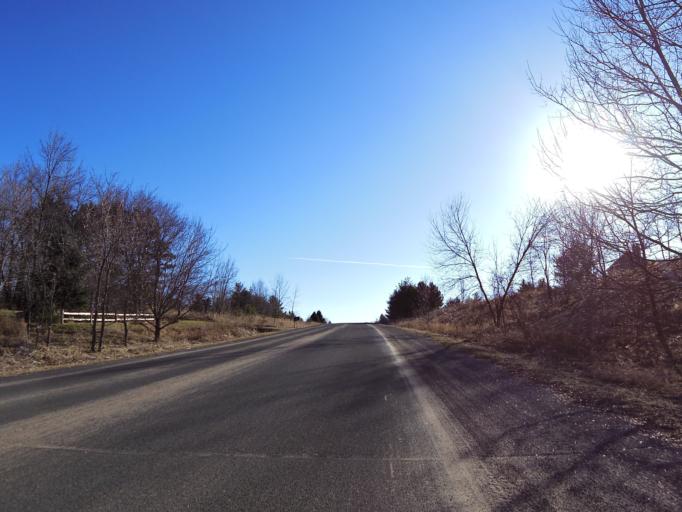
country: US
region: Minnesota
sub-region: Washington County
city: Bayport
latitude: 44.9901
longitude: -92.8042
